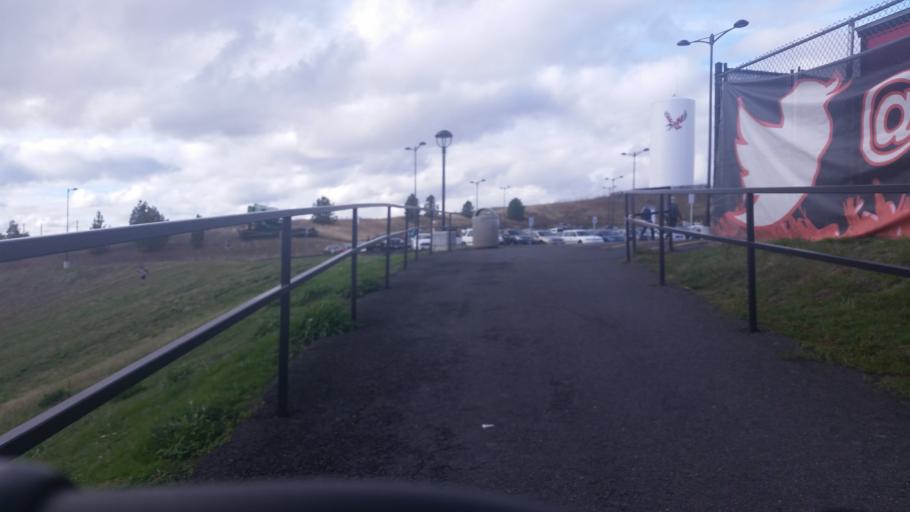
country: US
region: Washington
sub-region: Spokane County
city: Cheney
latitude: 47.4923
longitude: -117.5890
